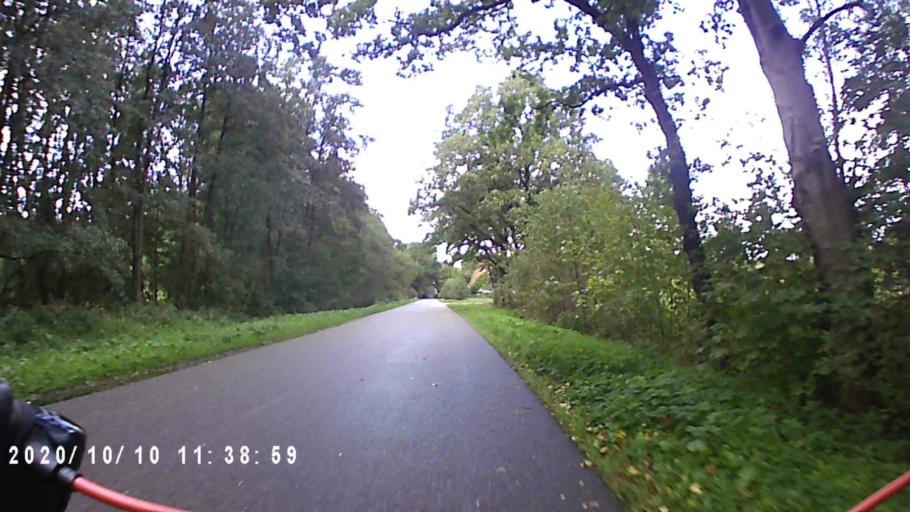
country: NL
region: Friesland
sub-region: Gemeente Smallingerland
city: Drachten
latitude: 53.0701
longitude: 6.1080
